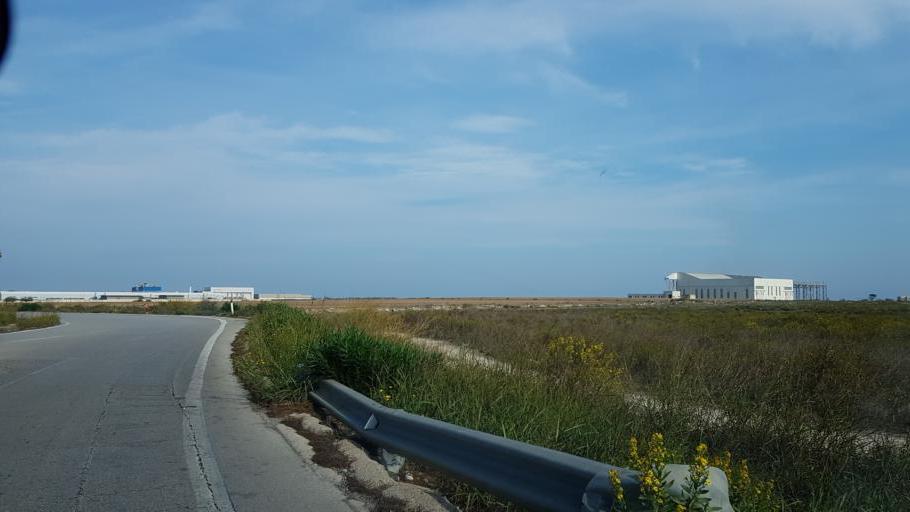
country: IT
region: Apulia
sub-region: Provincia di Brindisi
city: Brindisi
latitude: 40.6648
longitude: 17.9212
